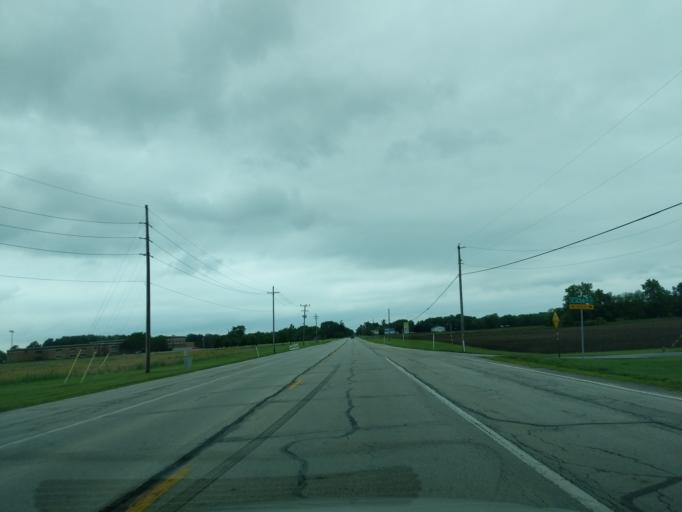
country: US
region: Indiana
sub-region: Hamilton County
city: Arcadia
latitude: 40.1615
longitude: -86.0132
